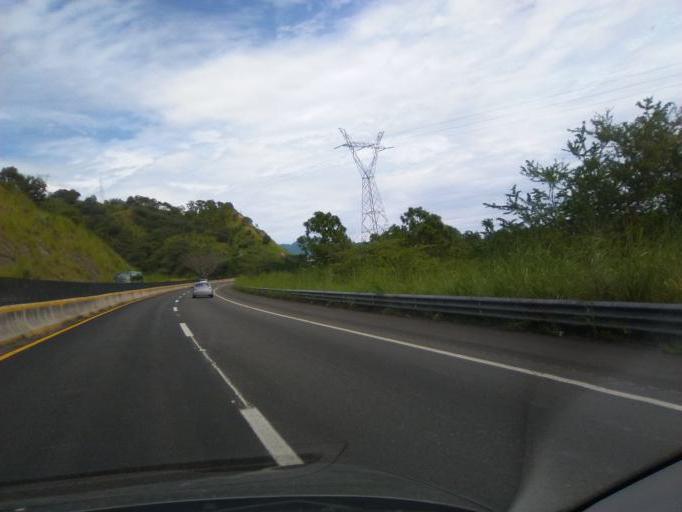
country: MX
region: Guerrero
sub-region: Chilpancingo de los Bravo
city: Cajelitos
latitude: 17.3096
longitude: -99.4935
